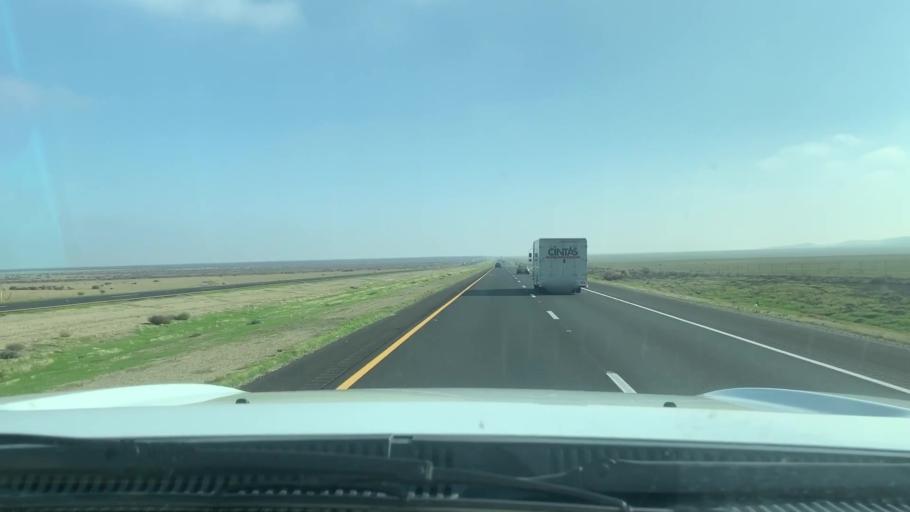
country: US
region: California
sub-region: Kern County
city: Lost Hills
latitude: 35.6281
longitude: -119.9932
